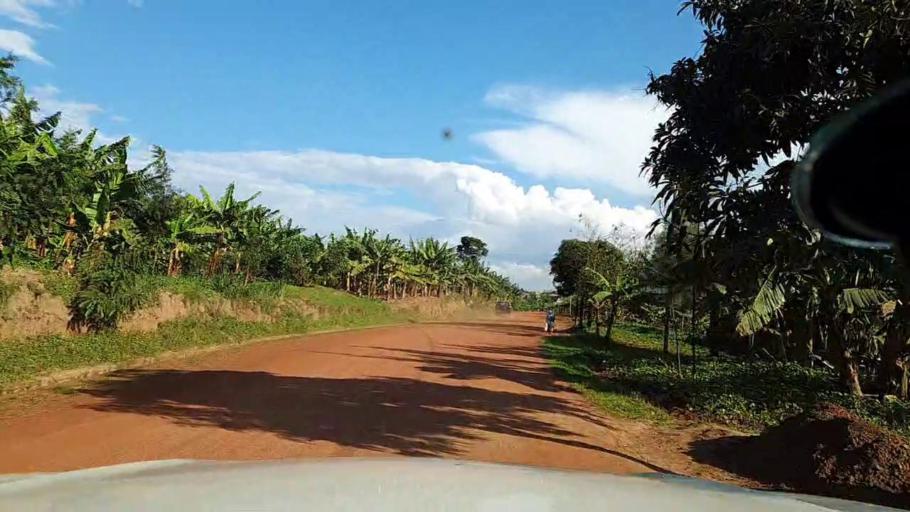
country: RW
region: Kigali
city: Kigali
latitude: -1.8603
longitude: 29.9181
